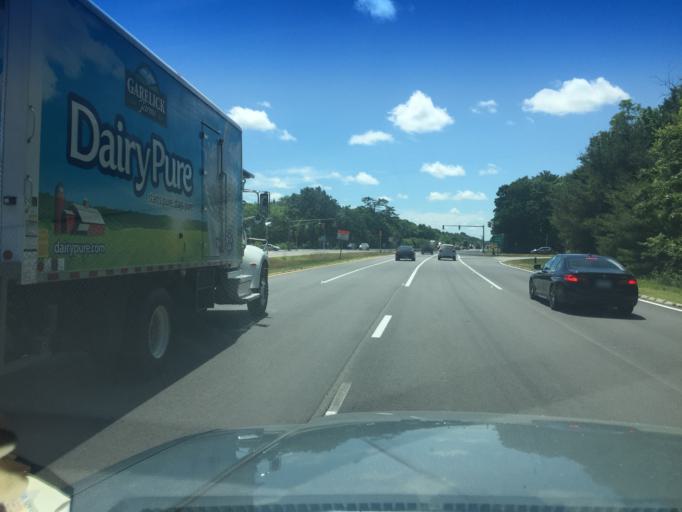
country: US
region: Massachusetts
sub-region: Bristol County
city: Mansfield
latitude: 42.0370
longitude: -71.2364
